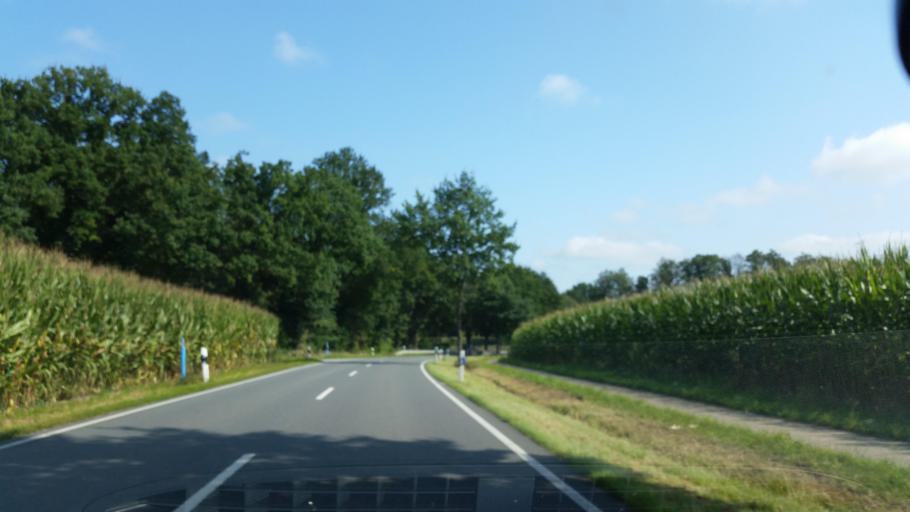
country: DE
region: Lower Saxony
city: Celle
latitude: 52.6563
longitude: 10.0887
